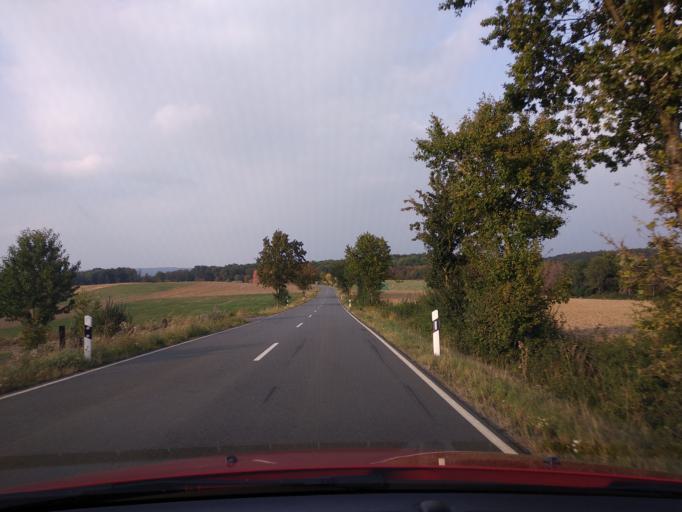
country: DE
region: North Rhine-Westphalia
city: Beverungen
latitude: 51.6359
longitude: 9.3405
